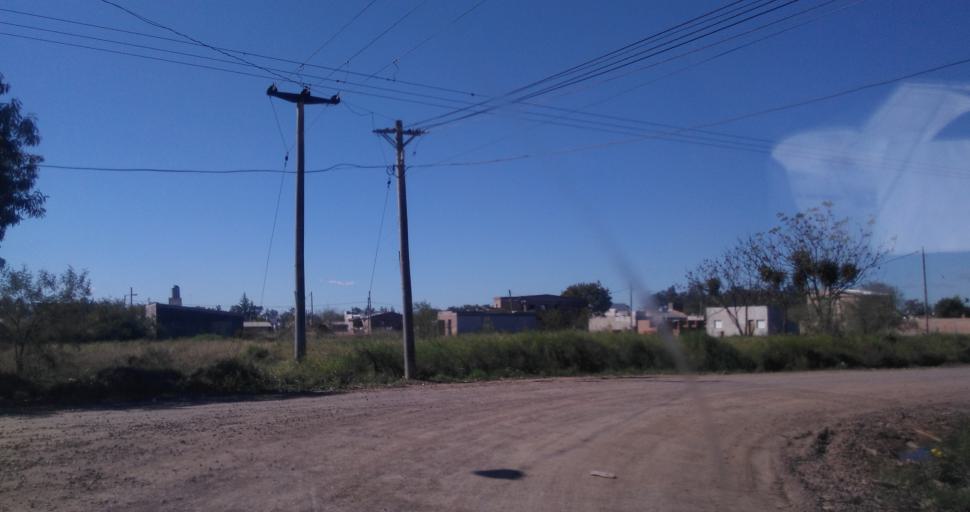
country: AR
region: Chaco
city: Fontana
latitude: -27.4466
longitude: -59.0349
